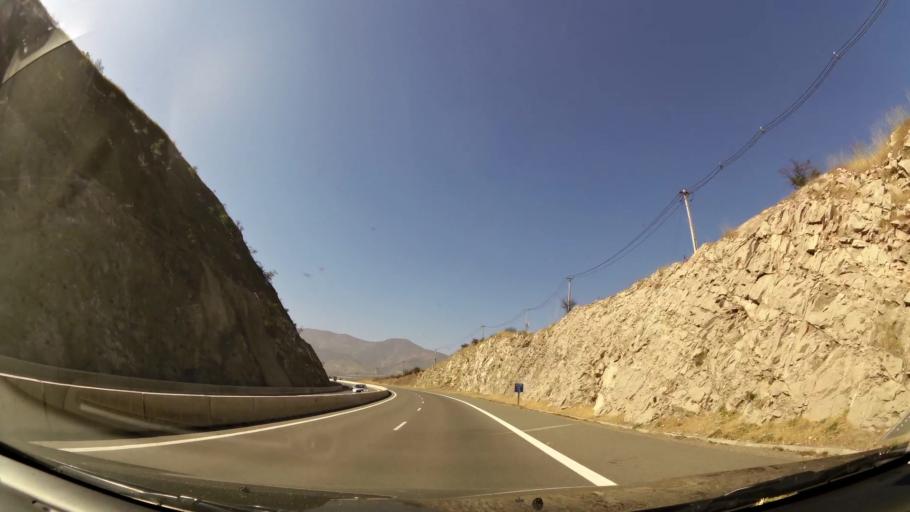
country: CL
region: Santiago Metropolitan
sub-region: Provincia de Chacabuco
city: Chicureo Abajo
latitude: -33.3105
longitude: -70.6524
